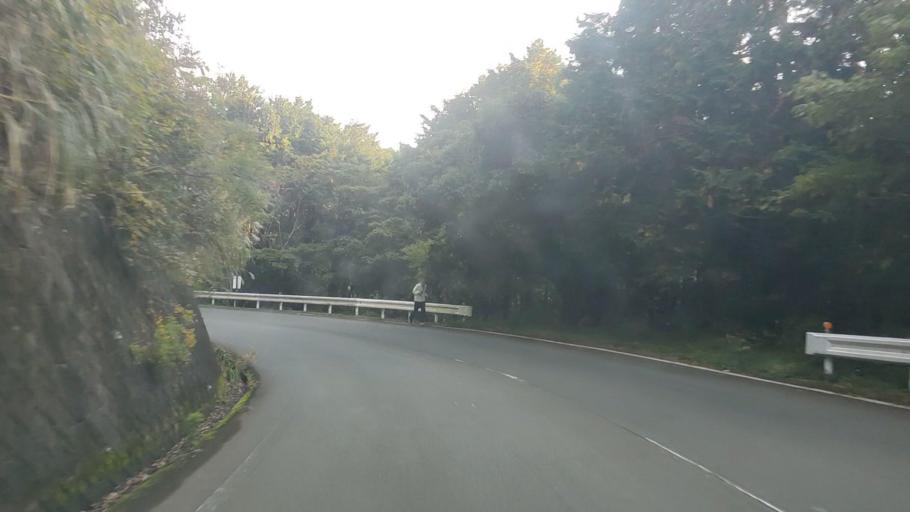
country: JP
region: Shizuoka
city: Mishima
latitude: 35.1479
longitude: 138.9378
